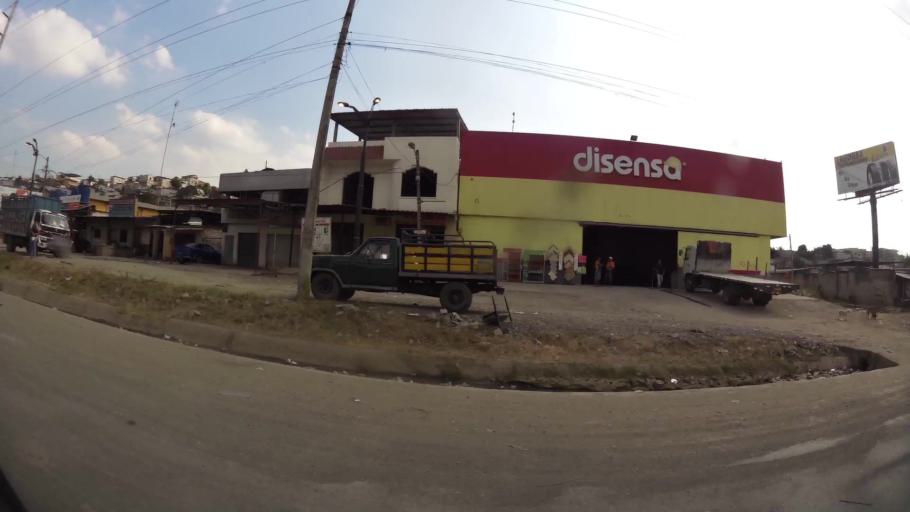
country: EC
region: Guayas
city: Santa Lucia
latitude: -2.1295
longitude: -79.9491
